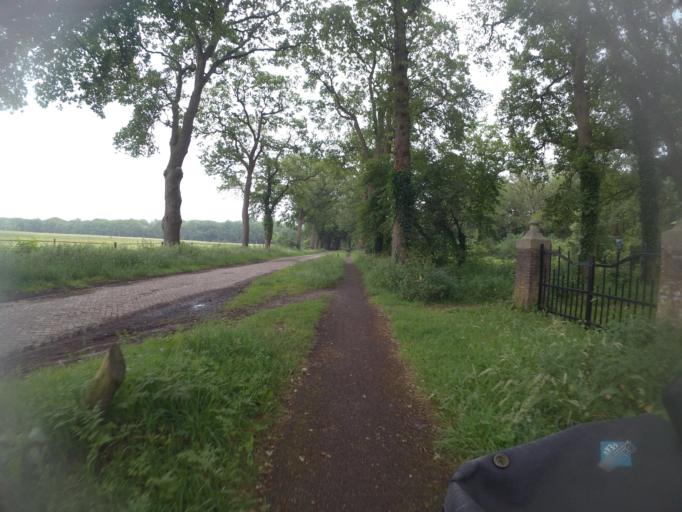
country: NL
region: Drenthe
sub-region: Gemeente Westerveld
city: Dwingeloo
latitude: 52.8172
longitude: 6.3444
